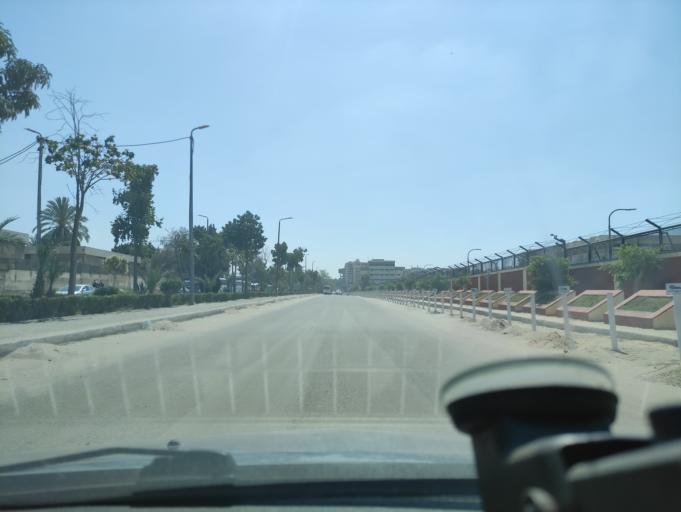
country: EG
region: Muhafazat al Qahirah
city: Cairo
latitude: 30.0443
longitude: 31.3455
